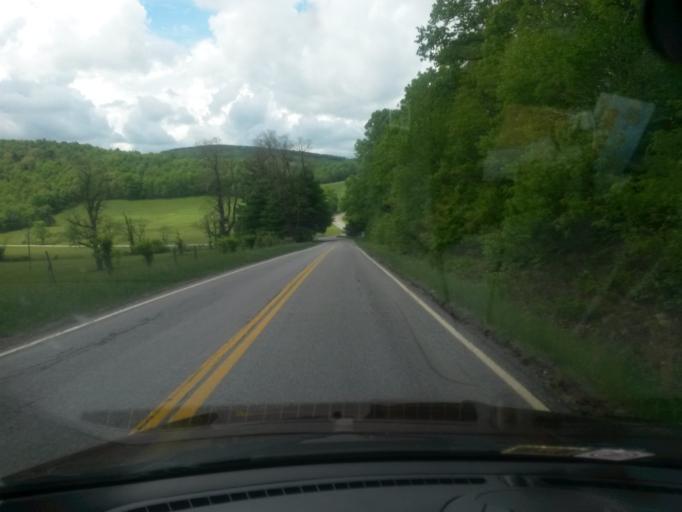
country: US
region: Virginia
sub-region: Floyd County
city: Floyd
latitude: 36.7734
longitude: -80.3896
